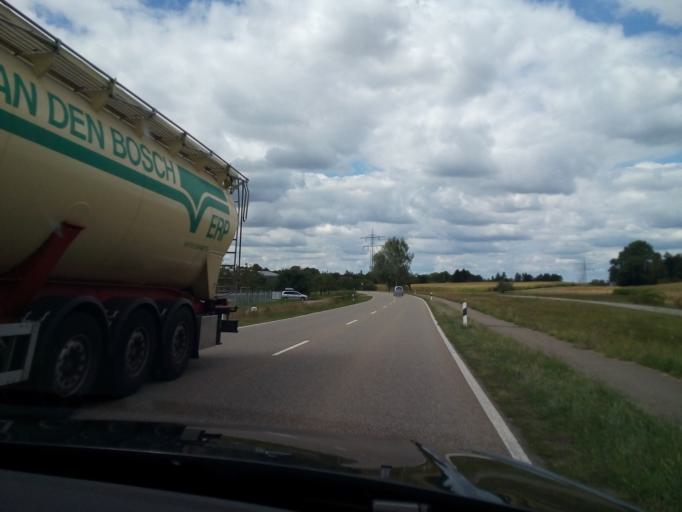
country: DE
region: Baden-Wuerttemberg
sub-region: Karlsruhe Region
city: Ottenhofen
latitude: 48.7276
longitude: 8.0971
